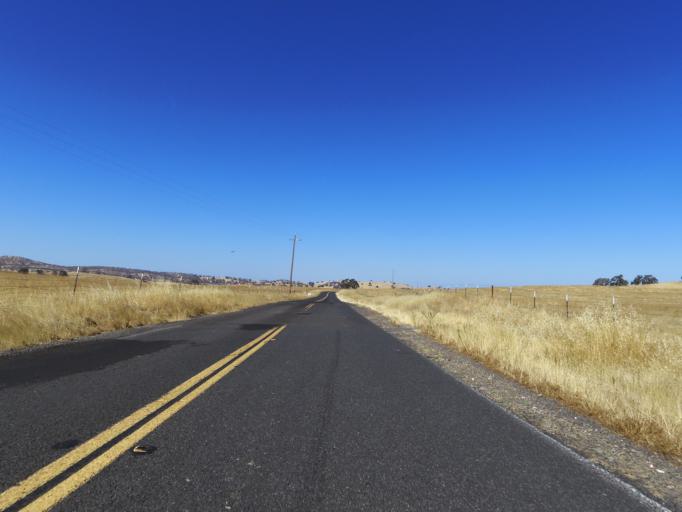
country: US
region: California
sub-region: Mariposa County
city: Mariposa
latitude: 37.4905
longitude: -120.1888
